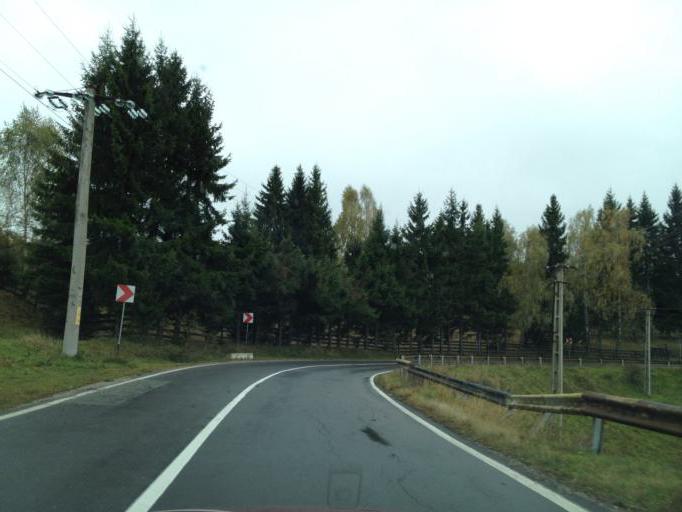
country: RO
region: Brasov
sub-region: Comuna Fundata
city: Fundata
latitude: 45.4649
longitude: 25.2938
